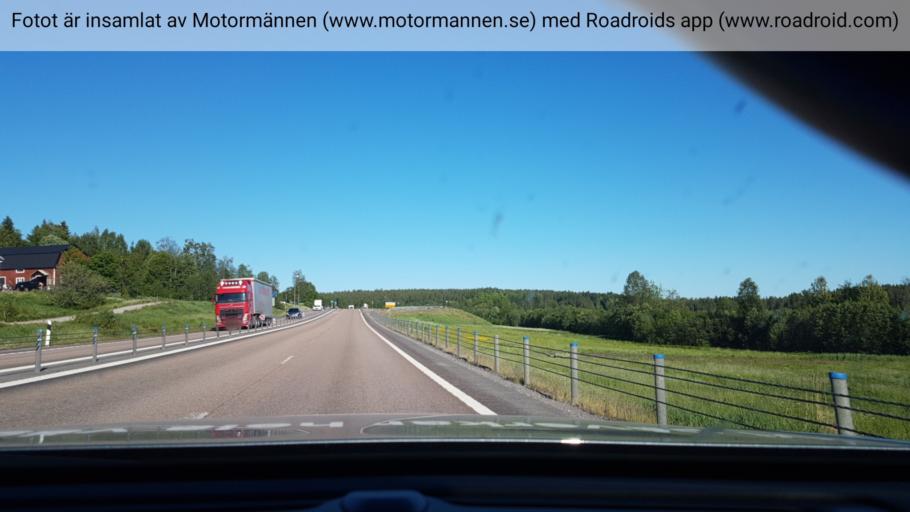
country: SE
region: Vaesternorrland
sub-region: Timra Kommun
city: Soraker
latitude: 62.5582
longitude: 17.6571
